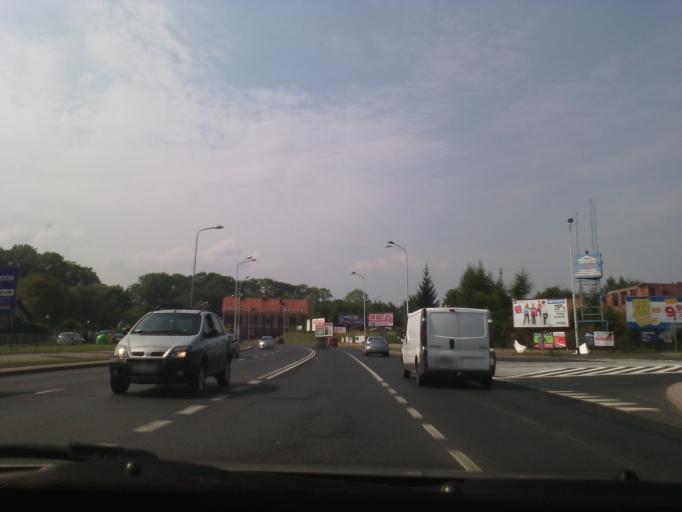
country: PL
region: Lower Silesian Voivodeship
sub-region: Powiat walbrzyski
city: Szczawno-Zdroj
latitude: 50.8187
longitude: 16.2789
